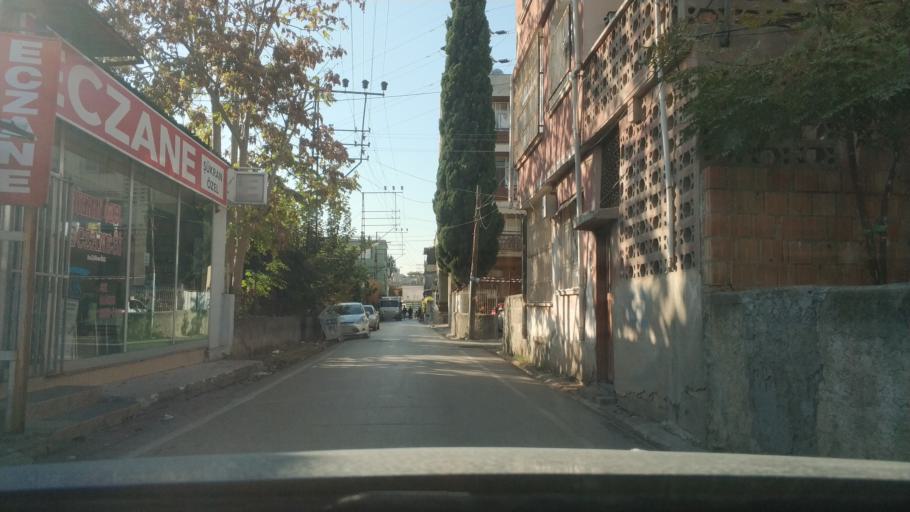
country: TR
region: Adana
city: Adana
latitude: 37.0088
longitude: 35.3135
